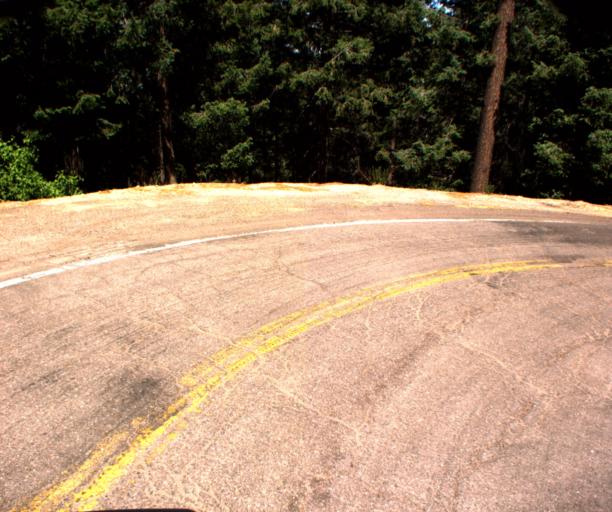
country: US
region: Arizona
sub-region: Graham County
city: Swift Trail Junction
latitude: 32.6310
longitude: -109.8250
